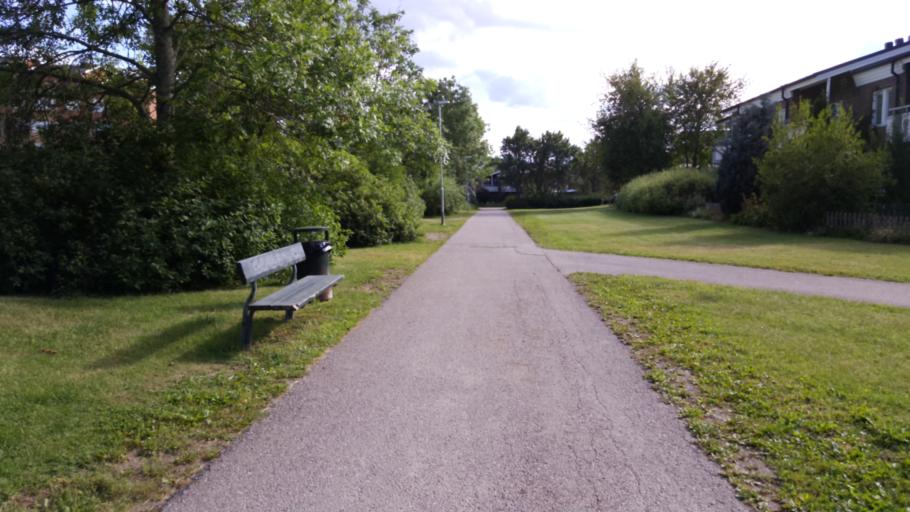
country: SE
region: Uppsala
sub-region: Uppsala Kommun
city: Gamla Uppsala
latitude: 59.8848
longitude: 17.6394
